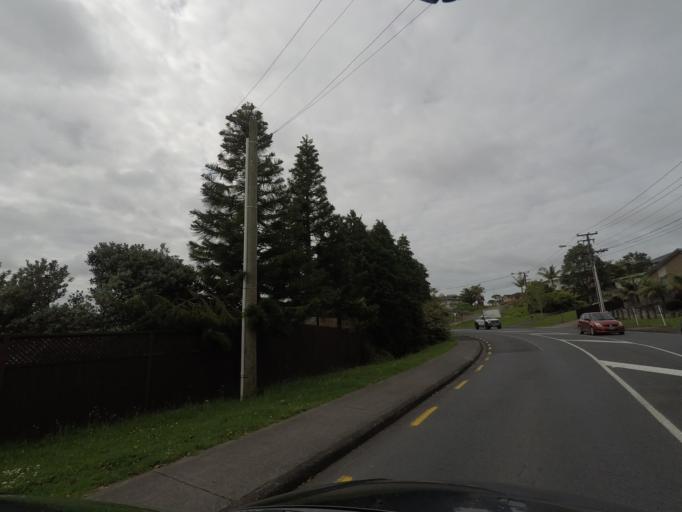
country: NZ
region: Auckland
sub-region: Auckland
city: Rosebank
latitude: -36.8523
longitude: 174.6100
